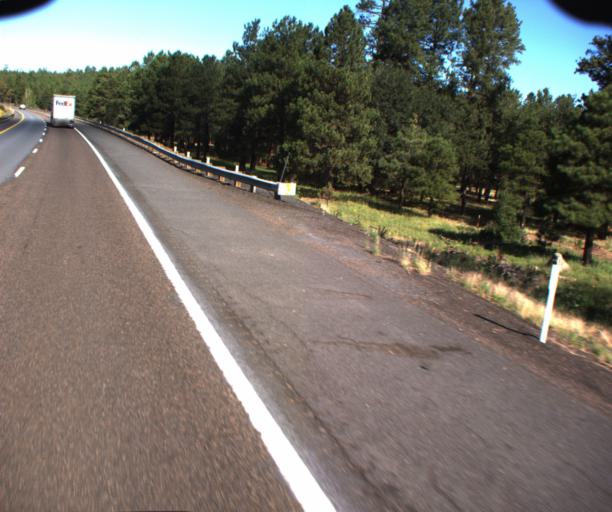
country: US
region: Arizona
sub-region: Coconino County
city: Parks
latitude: 35.2519
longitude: -111.8992
